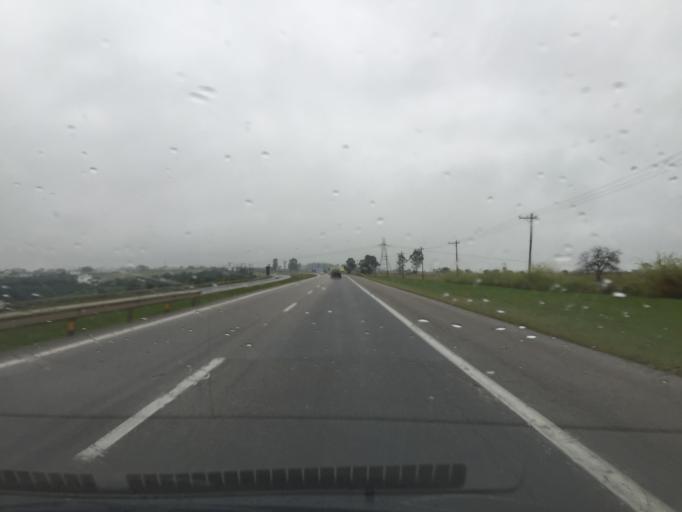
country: BR
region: Sao Paulo
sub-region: Itu
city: Itu
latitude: -23.2967
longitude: -47.3315
